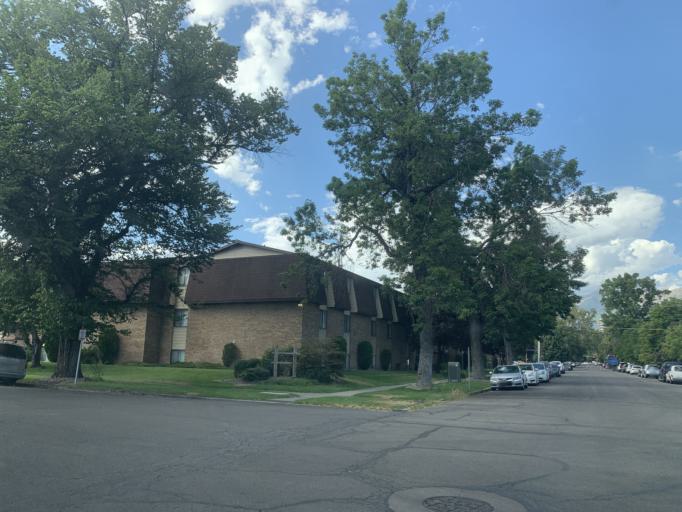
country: US
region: Utah
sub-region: Utah County
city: Provo
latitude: 40.2390
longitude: -111.6517
